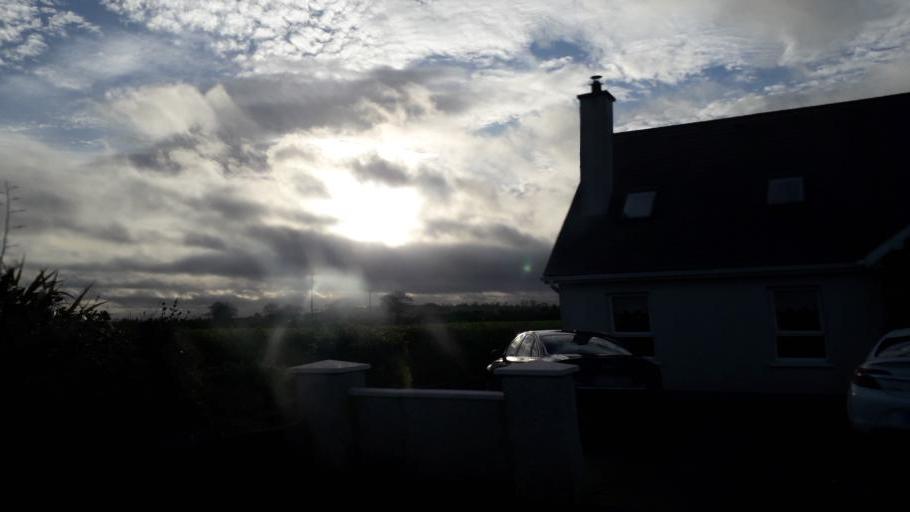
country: IE
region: Leinster
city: Balrothery
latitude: 53.5788
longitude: -6.1588
